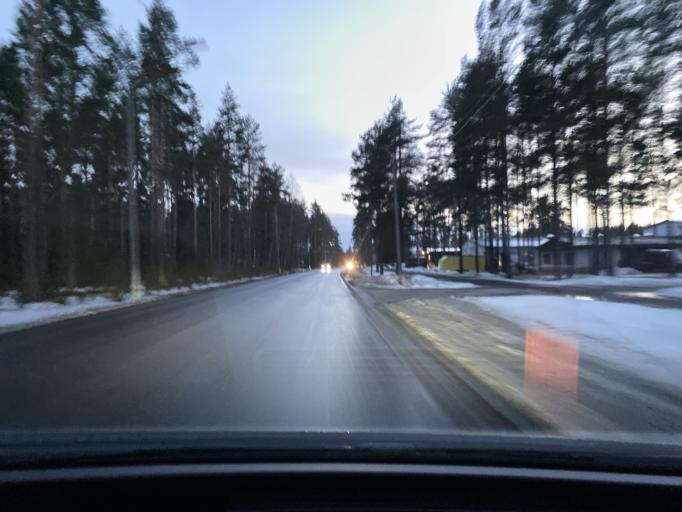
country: FI
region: Varsinais-Suomi
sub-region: Loimaa
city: Loimaa
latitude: 60.8489
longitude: 23.0359
